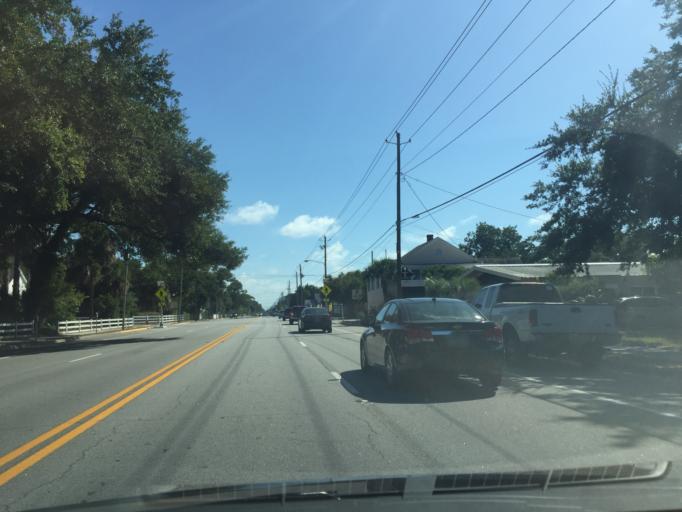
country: US
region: Georgia
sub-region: Chatham County
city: Tybee Island
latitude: 32.0043
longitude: -80.8445
